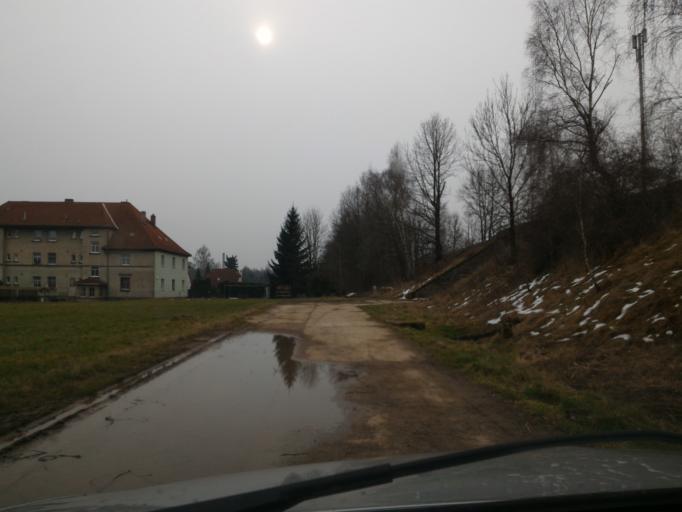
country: CZ
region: Ustecky
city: Varnsdorf
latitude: 50.8999
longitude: 14.6497
